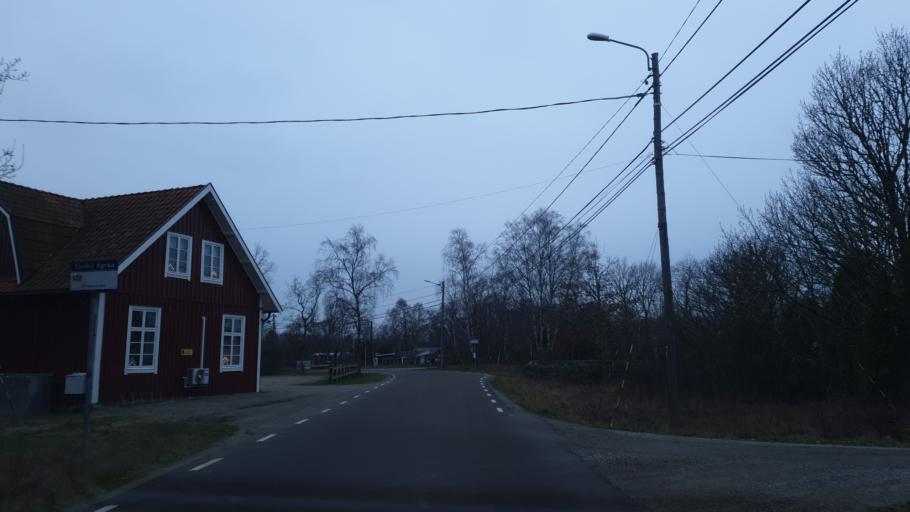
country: SE
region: Blekinge
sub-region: Karlskrona Kommun
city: Karlskrona
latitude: 56.1169
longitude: 15.6162
